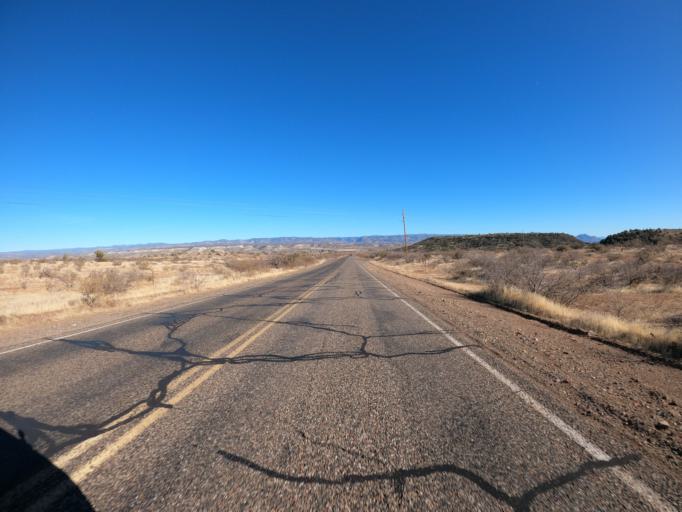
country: US
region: Arizona
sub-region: Yavapai County
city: Camp Verde
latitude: 34.5580
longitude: -111.8943
